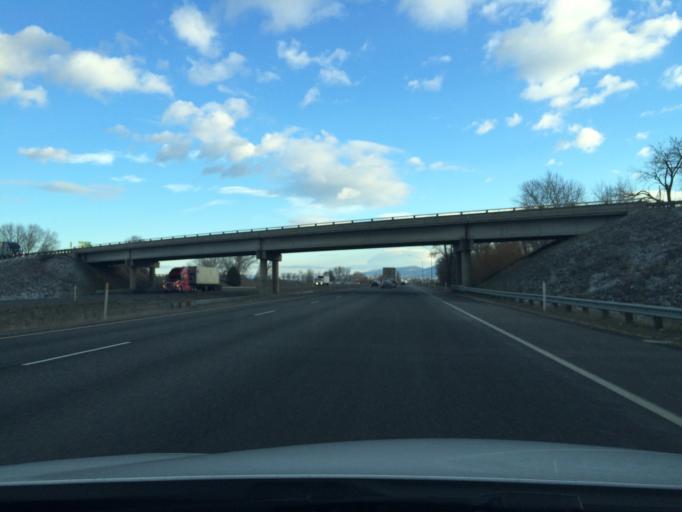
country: US
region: Washington
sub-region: Kittitas County
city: Ellensburg
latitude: 47.0064
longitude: -120.5920
